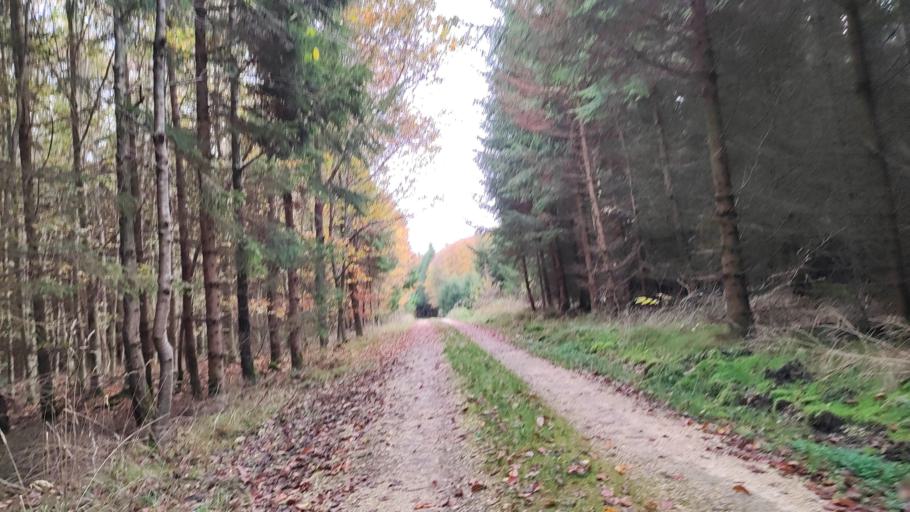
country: DE
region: Bavaria
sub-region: Swabia
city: Munsterhausen
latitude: 48.3223
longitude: 10.4894
